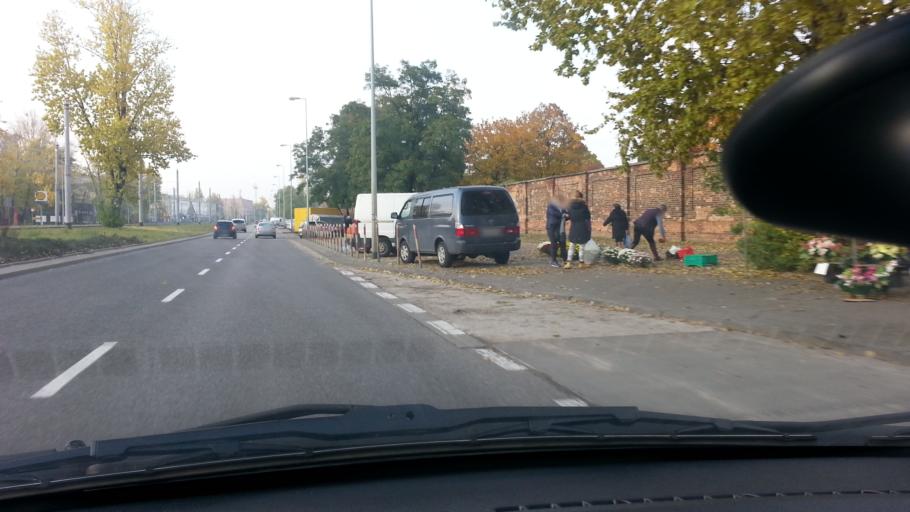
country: PL
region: Masovian Voivodeship
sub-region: Warszawa
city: Praga Polnoc
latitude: 52.2739
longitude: 21.0319
